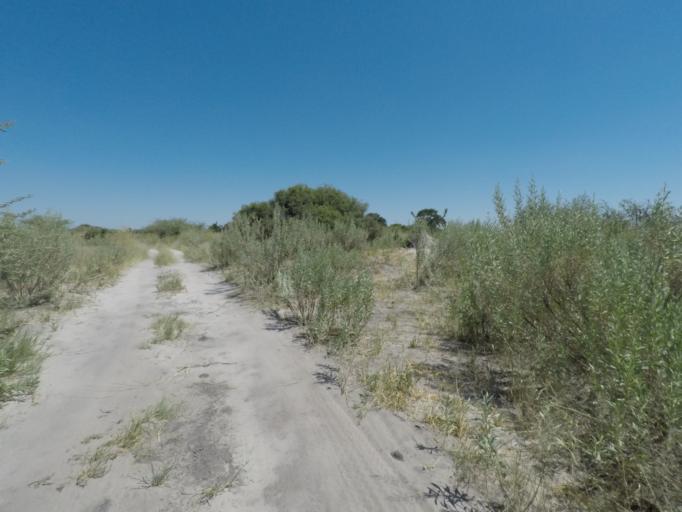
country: BW
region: North West
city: Maun
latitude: -19.4724
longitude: 23.5547
